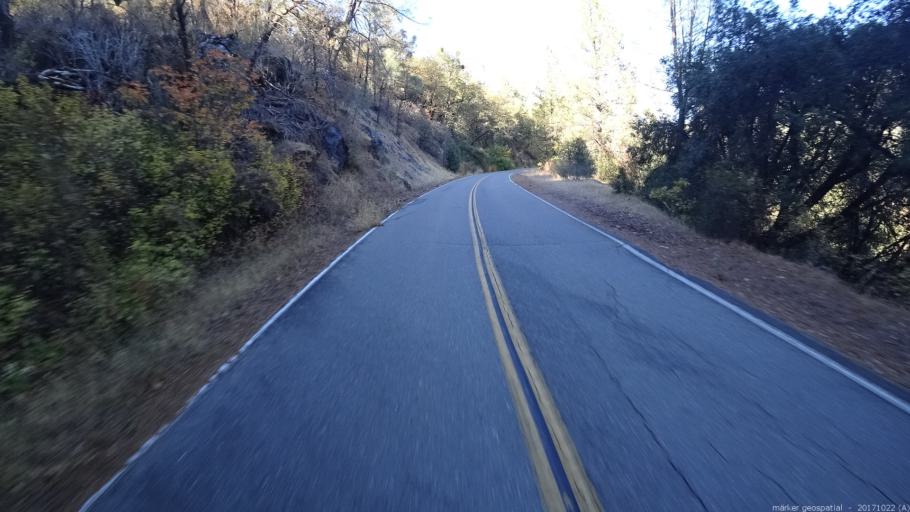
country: US
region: California
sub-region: Shasta County
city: Bella Vista
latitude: 40.8781
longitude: -122.2344
